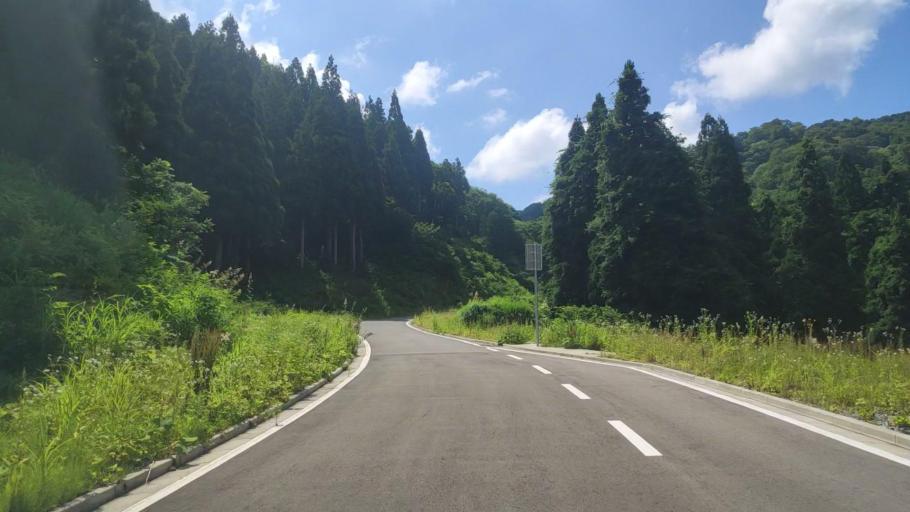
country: JP
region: Fukui
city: Katsuyama
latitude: 36.1562
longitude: 136.5267
